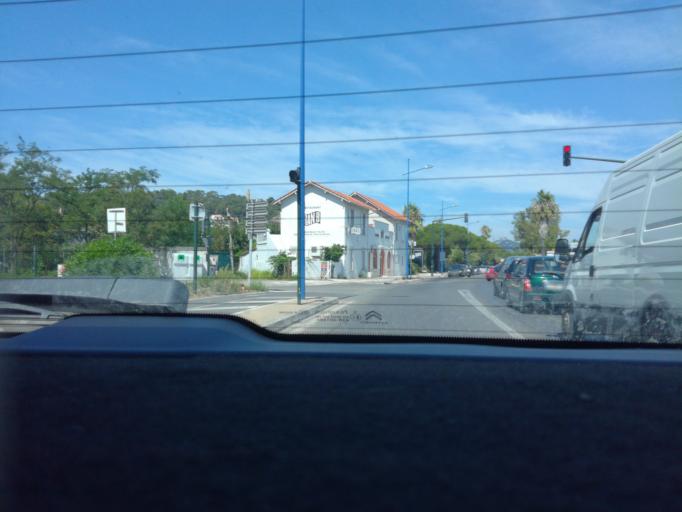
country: FR
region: Provence-Alpes-Cote d'Azur
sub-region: Departement du Var
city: Hyeres
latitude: 43.0948
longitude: 6.1369
